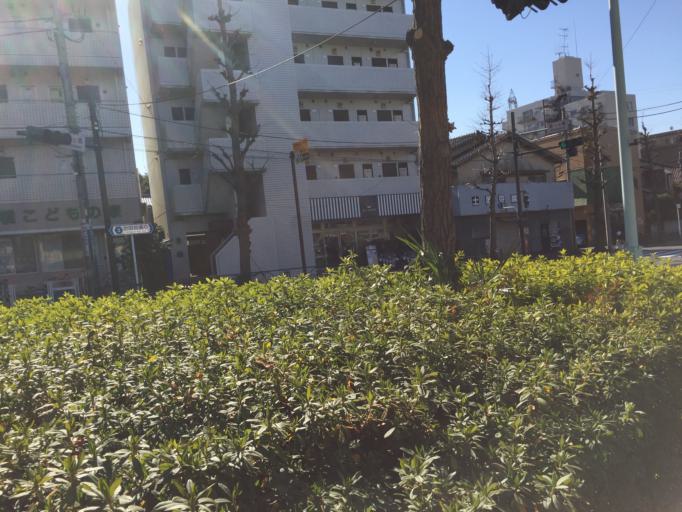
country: JP
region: Tokyo
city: Chofugaoka
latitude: 35.6329
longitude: 139.5849
